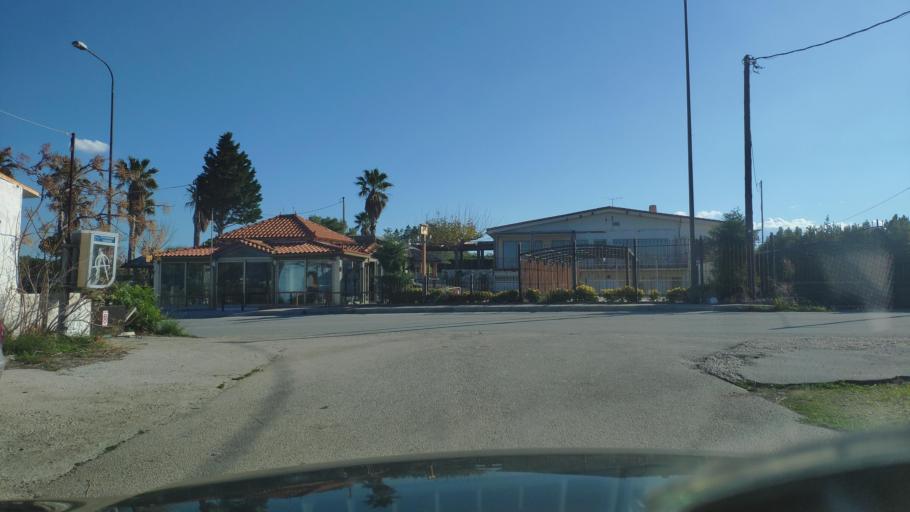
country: GR
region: Peloponnese
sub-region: Nomos Korinthias
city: Korinthos
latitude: 37.9492
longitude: 22.9617
